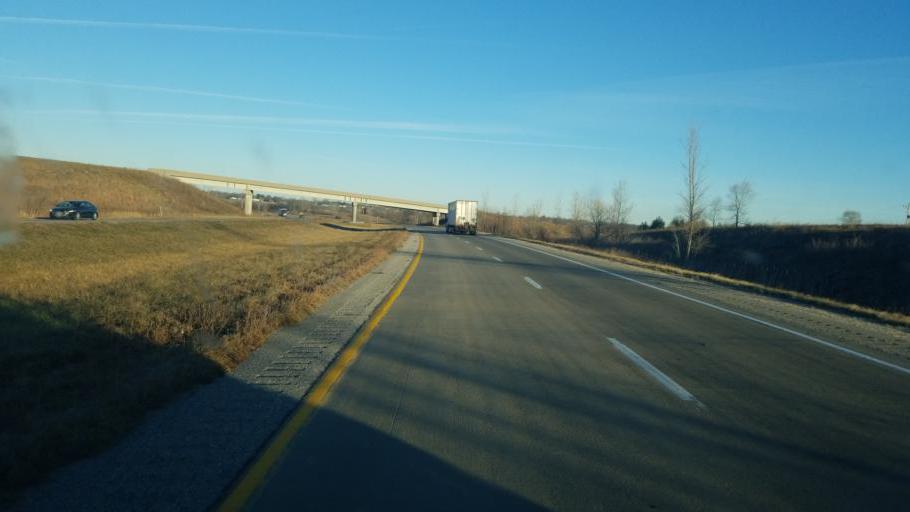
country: US
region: Iowa
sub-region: Mahaska County
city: Oskaloosa
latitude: 41.2586
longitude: -92.6417
